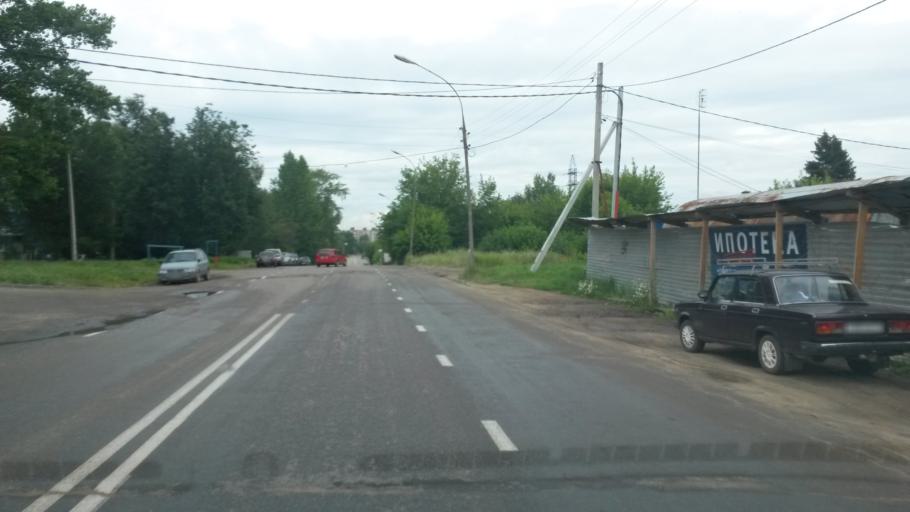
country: RU
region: Jaroslavl
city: Yaroslavl
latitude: 57.5809
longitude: 39.8658
